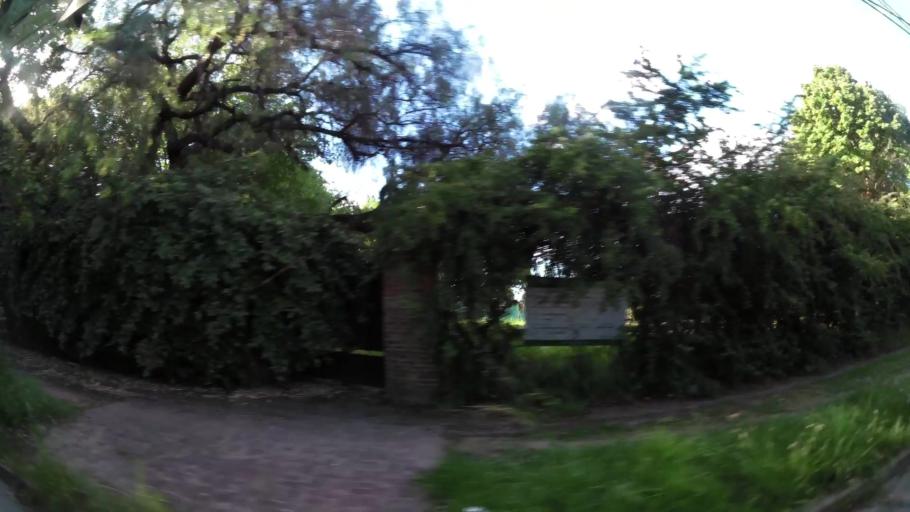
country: AR
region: Buenos Aires
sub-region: Partido de San Isidro
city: San Isidro
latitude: -34.4862
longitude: -58.5525
